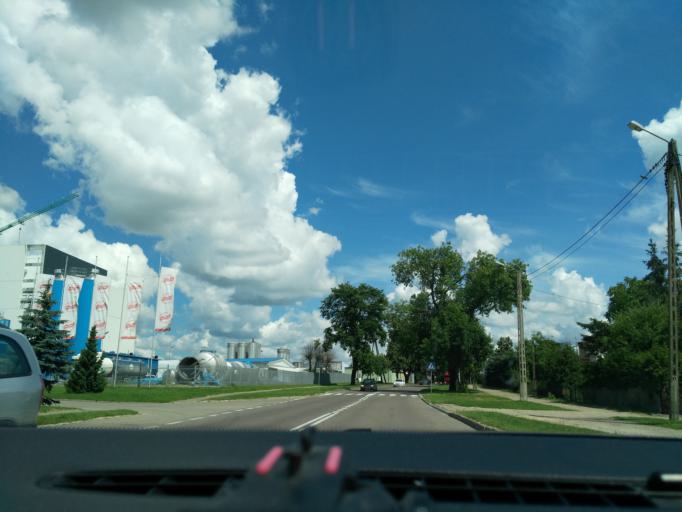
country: PL
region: Podlasie
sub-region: Powiat bielski
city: Bielsk Podlaski
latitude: 52.7561
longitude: 23.1753
